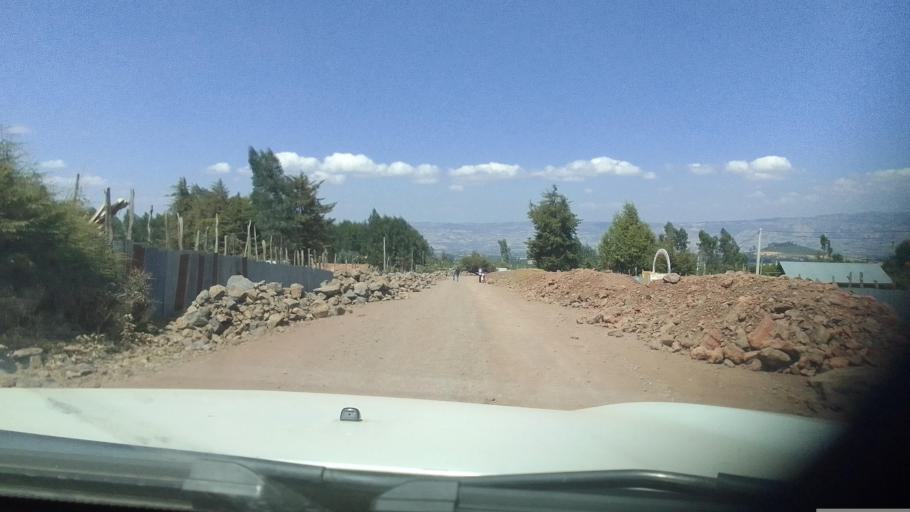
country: ET
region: Oromiya
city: Hagere Hiywet
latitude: 8.8600
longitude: 37.8909
